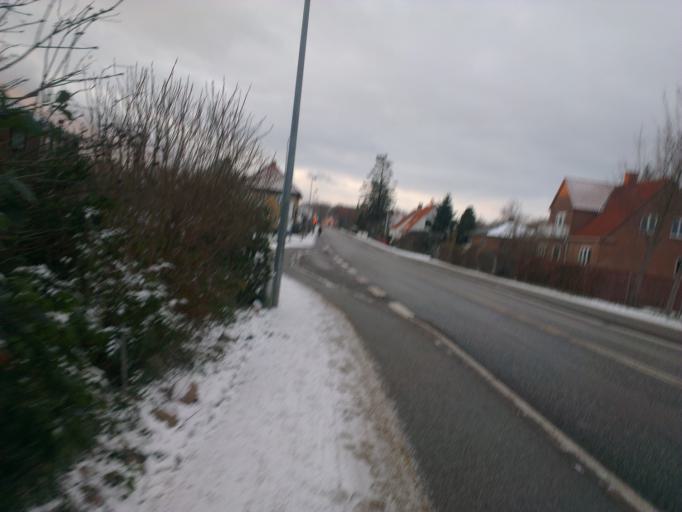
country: DK
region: Capital Region
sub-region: Frederikssund Kommune
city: Jaegerspris
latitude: 55.8552
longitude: 11.9903
